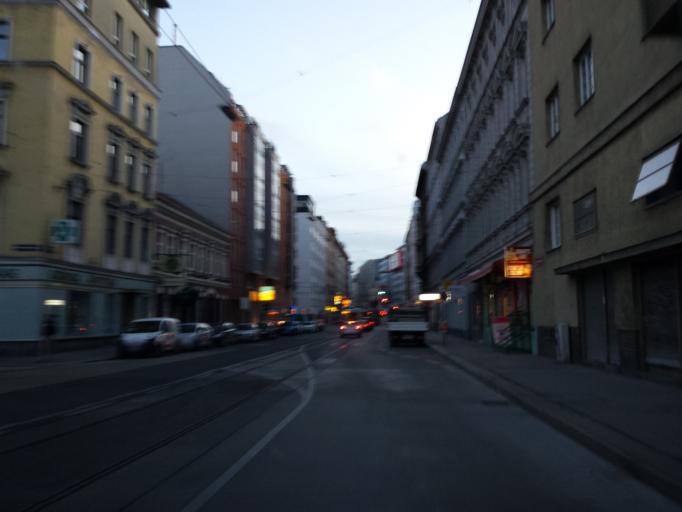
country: AT
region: Vienna
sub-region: Wien Stadt
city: Vienna
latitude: 48.1959
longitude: 16.4091
